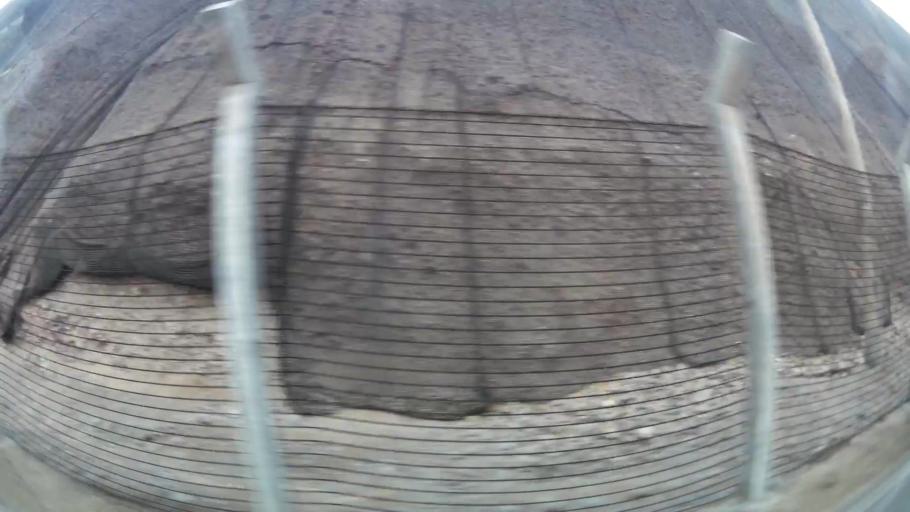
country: PE
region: Lima
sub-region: Lima
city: San Isidro
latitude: -12.1261
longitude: -77.0381
